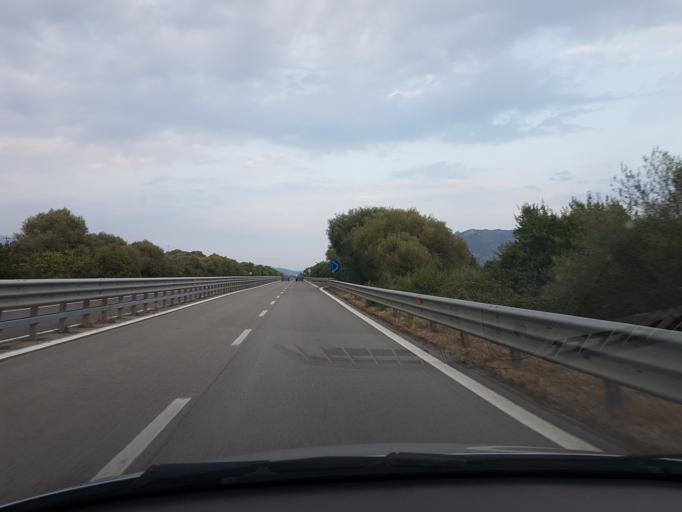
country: IT
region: Sardinia
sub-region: Provincia di Nuoro
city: Orune
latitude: 40.3747
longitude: 9.4053
